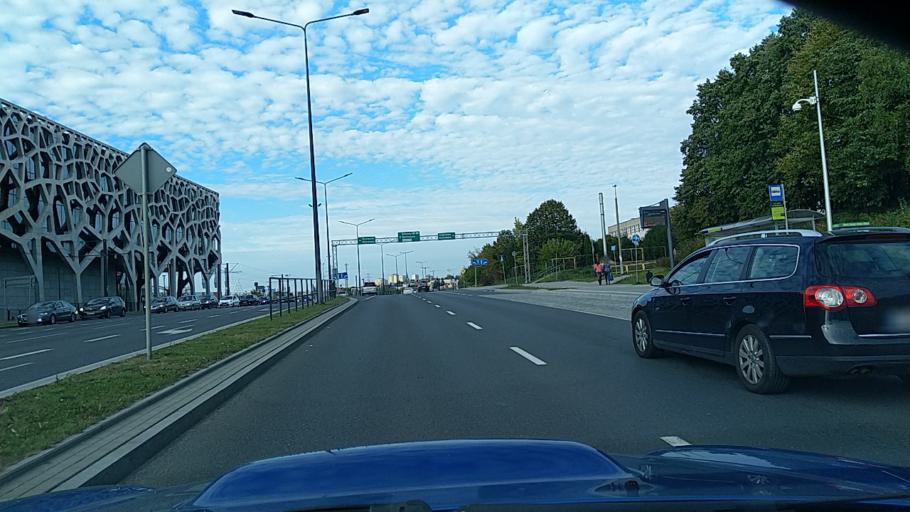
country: PL
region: Warmian-Masurian Voivodeship
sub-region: Powiat olsztynski
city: Olsztyn
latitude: 53.7535
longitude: 20.4863
